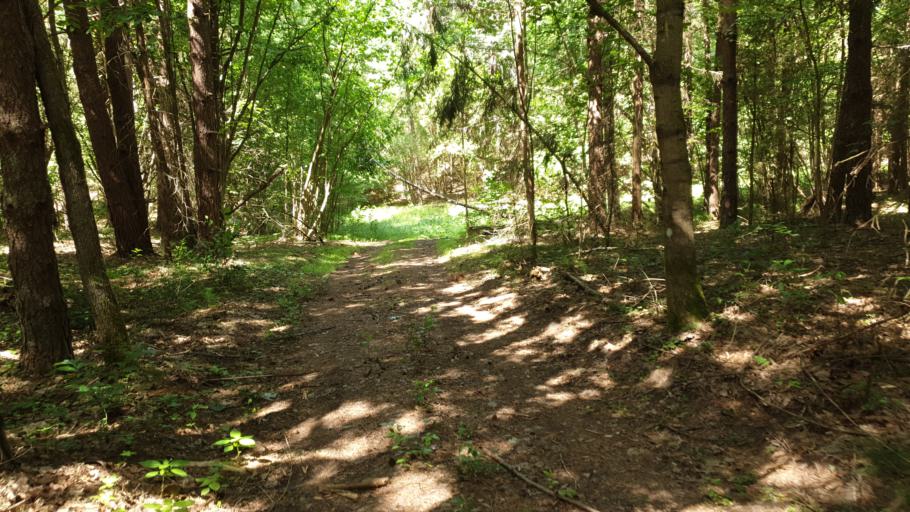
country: LT
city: Grigiskes
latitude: 54.7799
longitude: 24.9922
